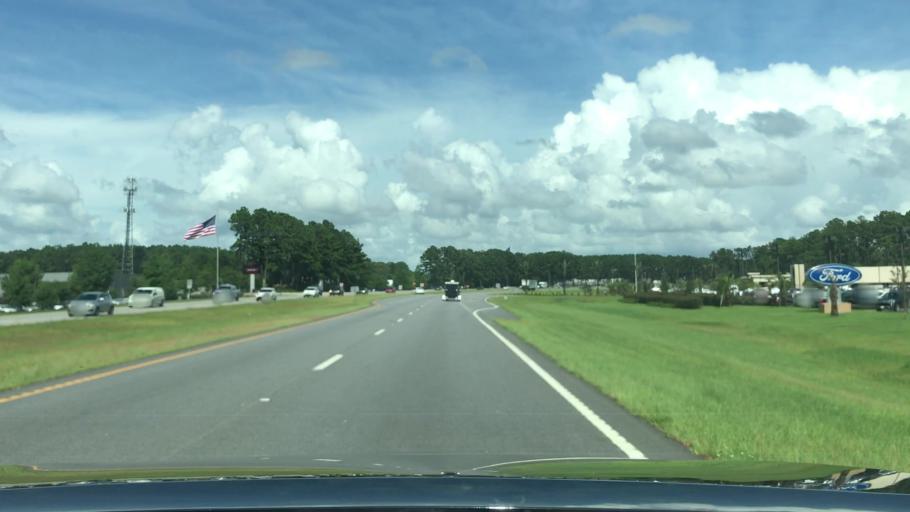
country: US
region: South Carolina
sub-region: Jasper County
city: Hardeeville
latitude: 32.3106
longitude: -80.9869
